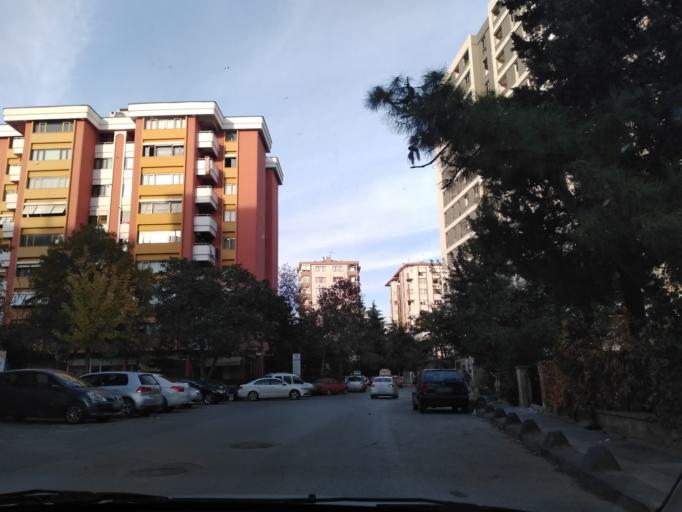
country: TR
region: Istanbul
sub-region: Atasehir
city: Atasehir
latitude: 40.9734
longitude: 29.0926
